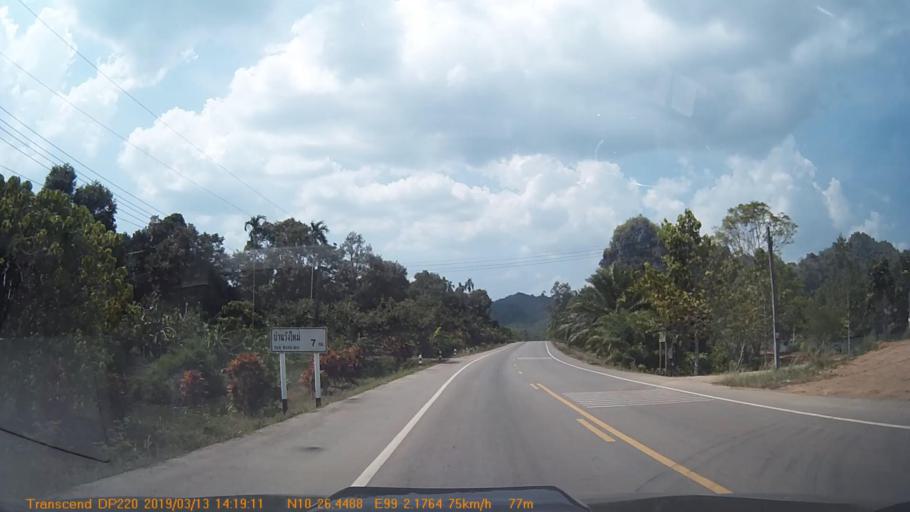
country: TH
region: Chumphon
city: Chumphon
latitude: 10.4291
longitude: 99.0401
